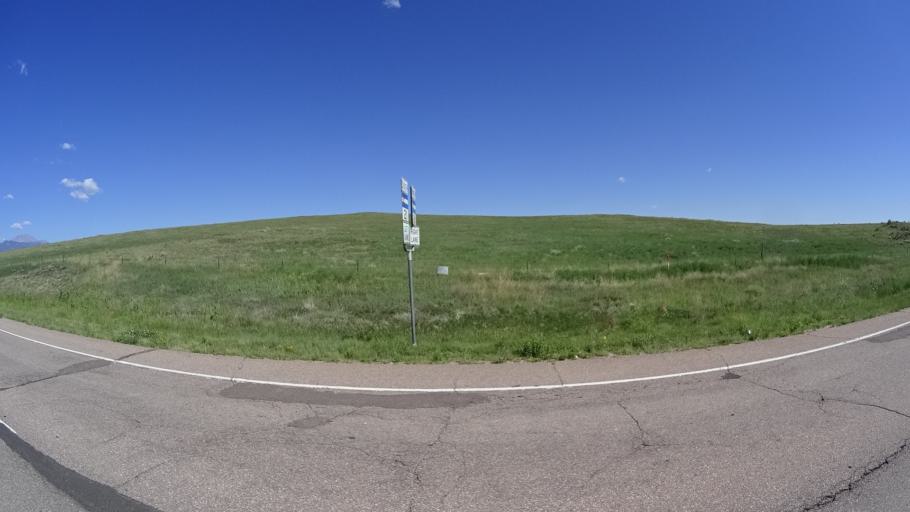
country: US
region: Colorado
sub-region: El Paso County
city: Security-Widefield
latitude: 38.7613
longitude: -104.6796
